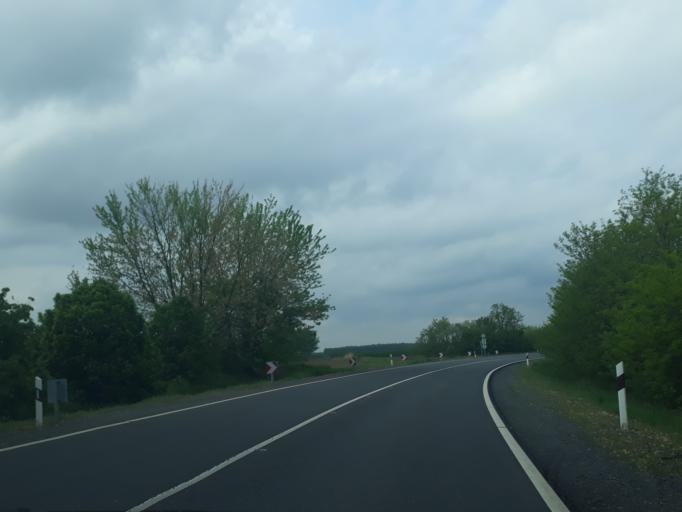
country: HU
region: Szabolcs-Szatmar-Bereg
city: Patroha
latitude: 48.1584
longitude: 22.0276
